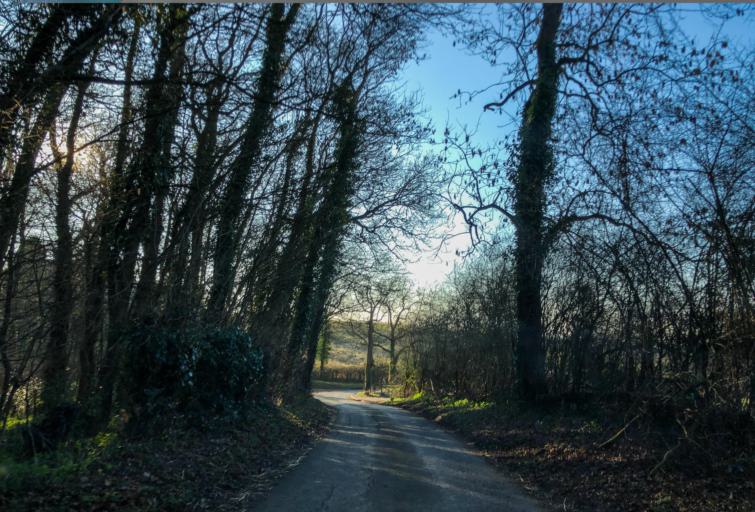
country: GB
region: England
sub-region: Warwickshire
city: Wellesbourne Mountford
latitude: 52.1992
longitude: -1.5276
